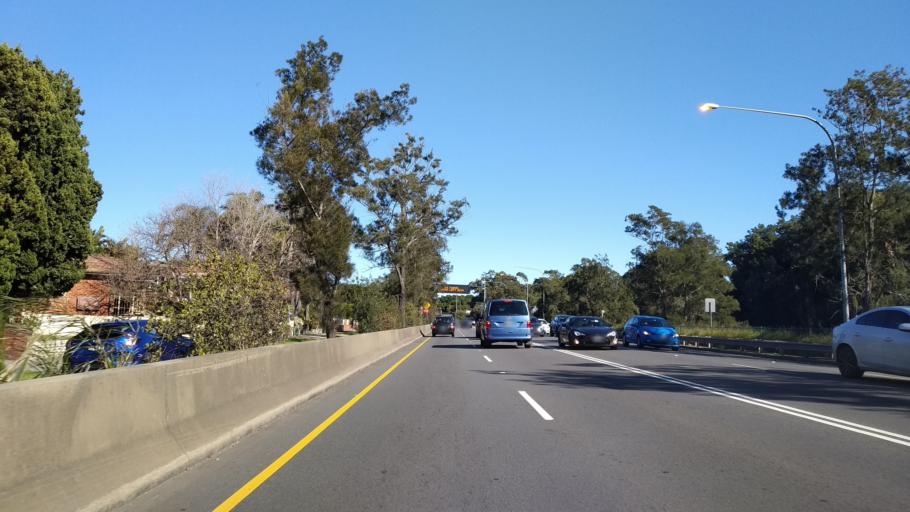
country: AU
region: New South Wales
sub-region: Canada Bay
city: Wareemba
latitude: -33.8715
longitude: 151.1404
